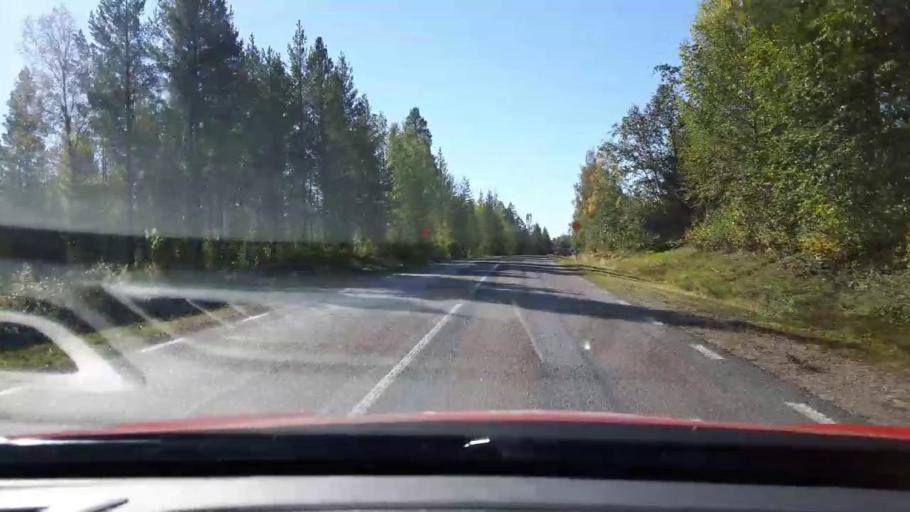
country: SE
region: Jaemtland
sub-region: Harjedalens Kommun
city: Sveg
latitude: 62.1297
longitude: 14.1658
